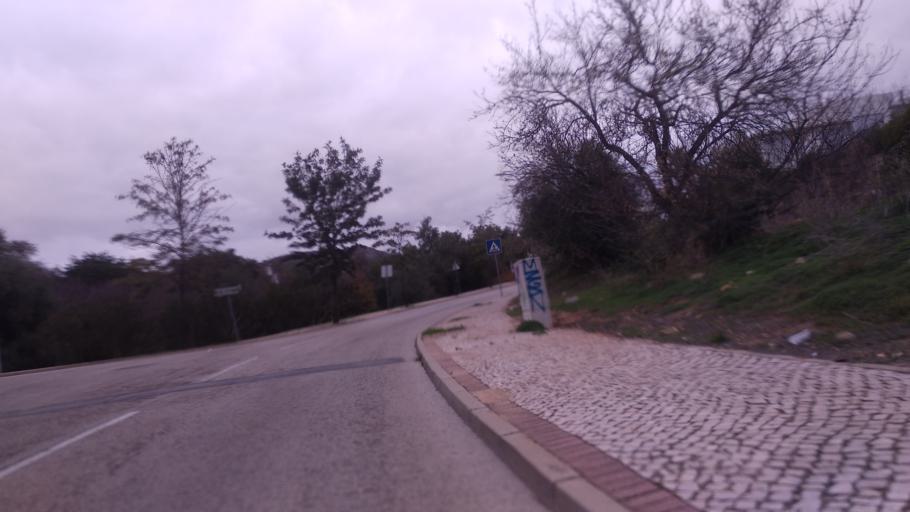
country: PT
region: Faro
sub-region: Faro
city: Santa Barbara de Nexe
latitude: 37.1022
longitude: -7.9654
